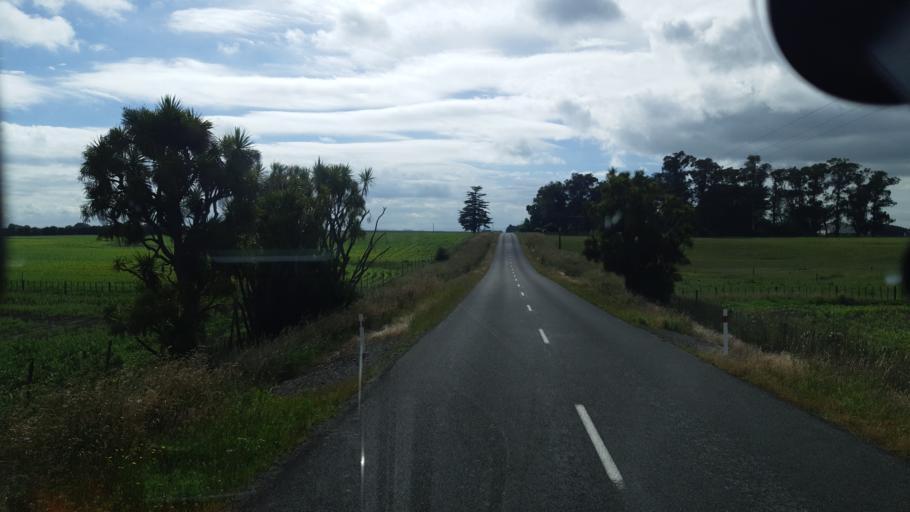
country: NZ
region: Manawatu-Wanganui
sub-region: Rangitikei District
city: Bulls
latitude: -40.0107
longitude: 175.4319
